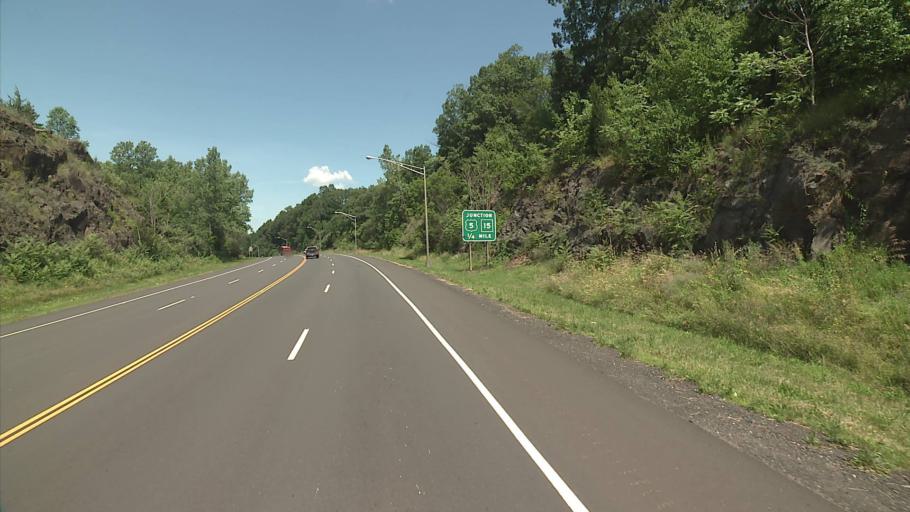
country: US
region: Connecticut
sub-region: Hartford County
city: Kensington
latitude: 41.6230
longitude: -72.7351
